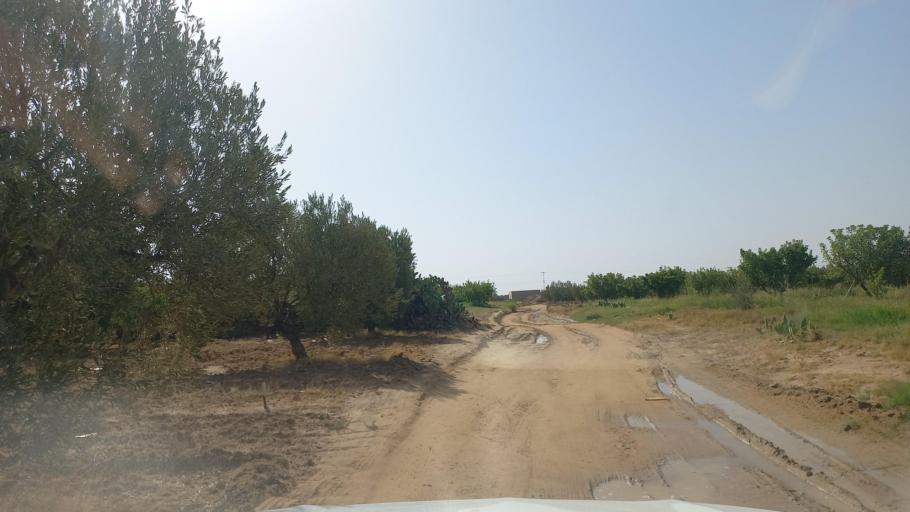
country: TN
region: Al Qasrayn
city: Kasserine
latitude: 35.2424
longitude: 9.0356
